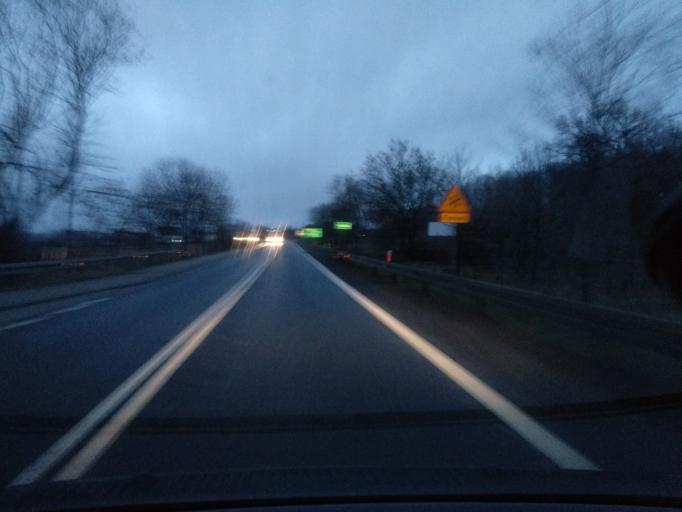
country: PL
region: Lower Silesian Voivodeship
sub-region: Powiat sredzki
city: Malczyce
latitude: 51.1930
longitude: 16.5048
